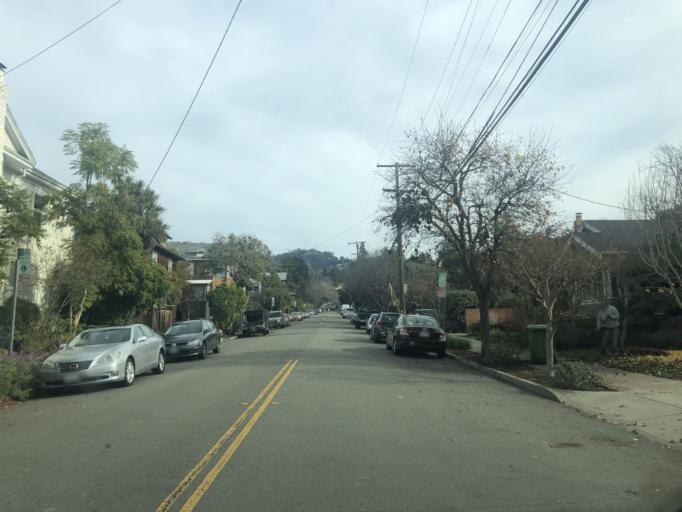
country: US
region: California
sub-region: Alameda County
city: Berkeley
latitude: 37.8560
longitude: -122.2505
